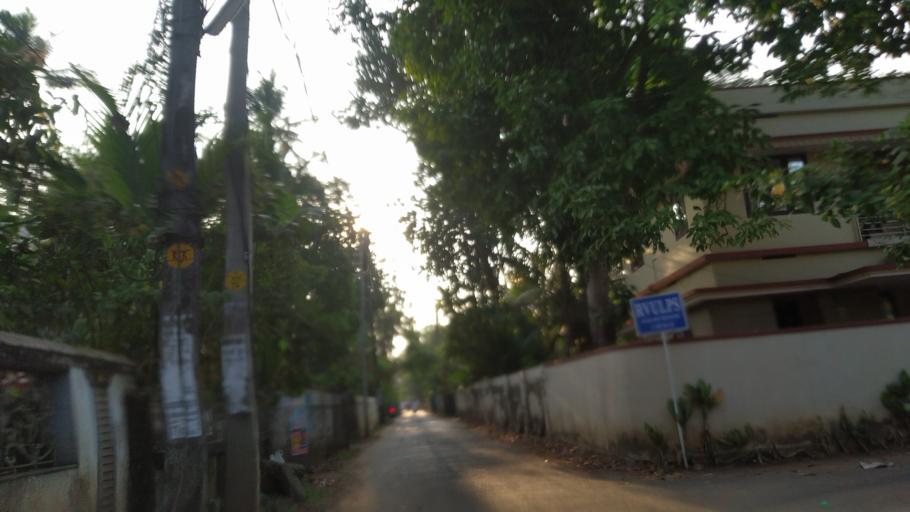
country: IN
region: Kerala
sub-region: Thrissur District
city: Kodungallur
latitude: 10.1348
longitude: 76.1943
